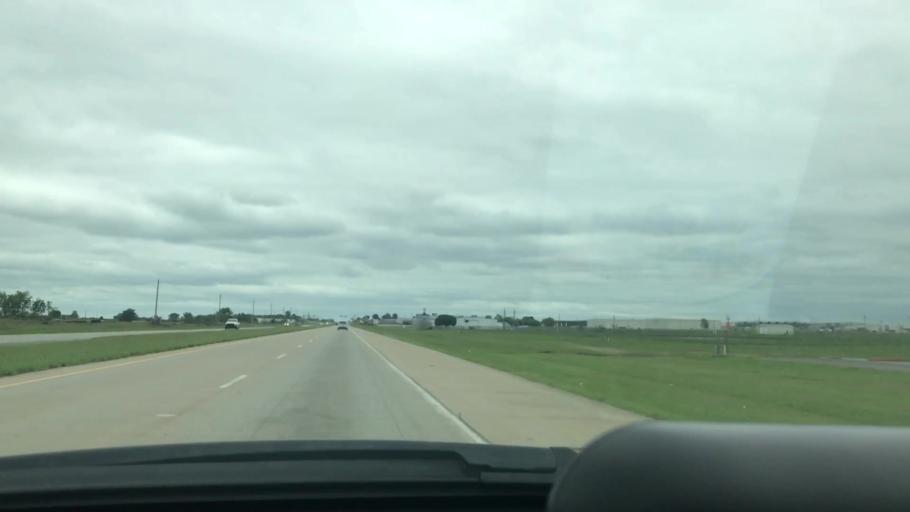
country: US
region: Oklahoma
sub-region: Mayes County
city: Chouteau
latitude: 36.2318
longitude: -95.3392
